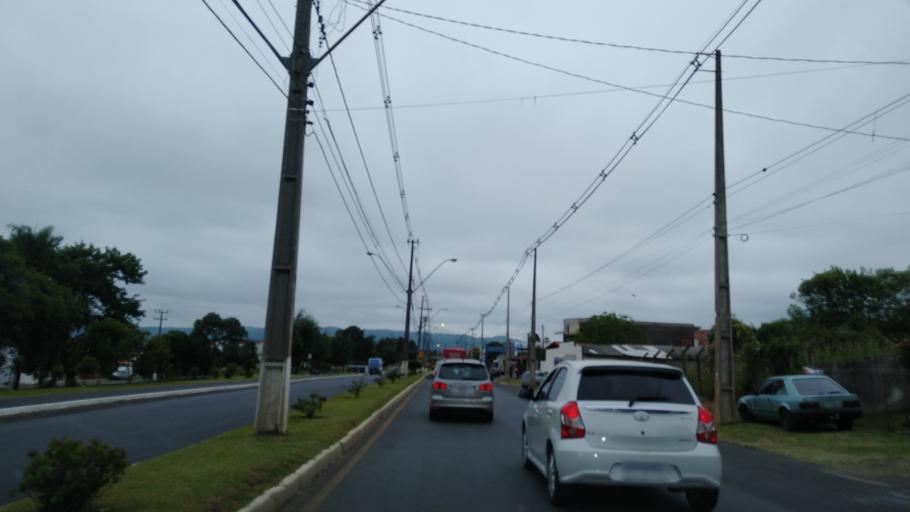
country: BR
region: Santa Catarina
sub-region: Porto Uniao
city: Porto Uniao
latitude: -26.2514
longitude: -51.0819
